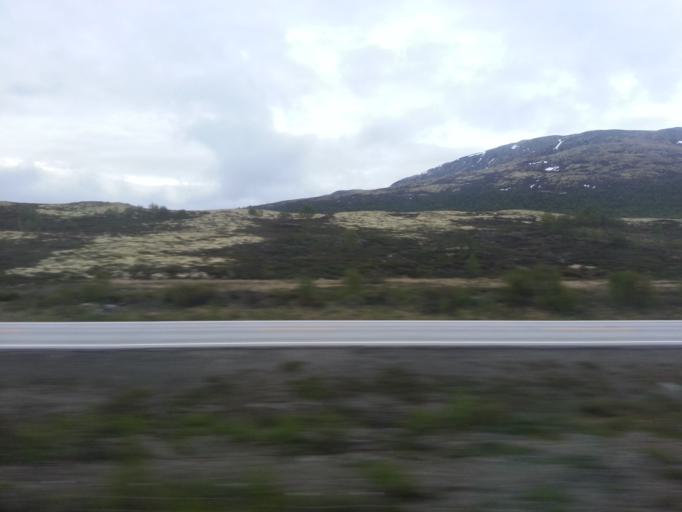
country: NO
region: Sor-Trondelag
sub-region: Oppdal
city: Oppdal
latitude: 62.2608
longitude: 9.5582
